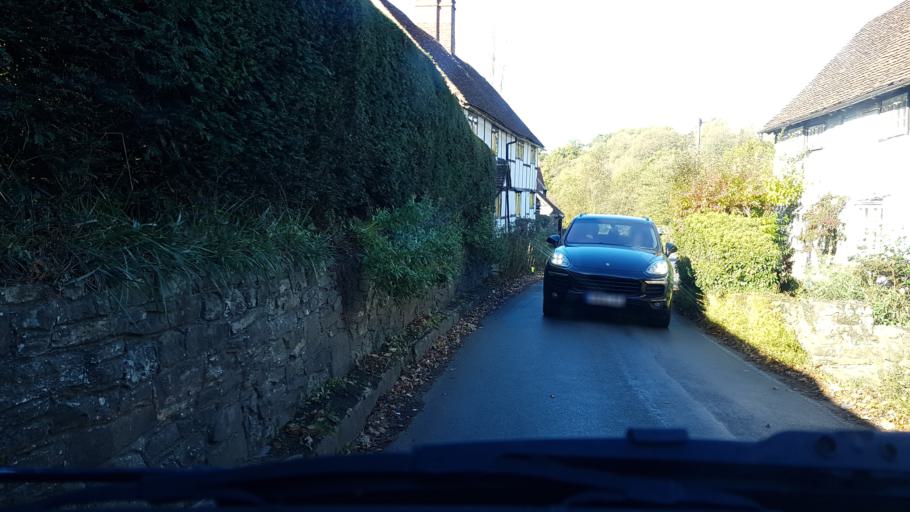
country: GB
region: England
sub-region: Surrey
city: East Horsley
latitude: 51.2014
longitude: -0.4197
